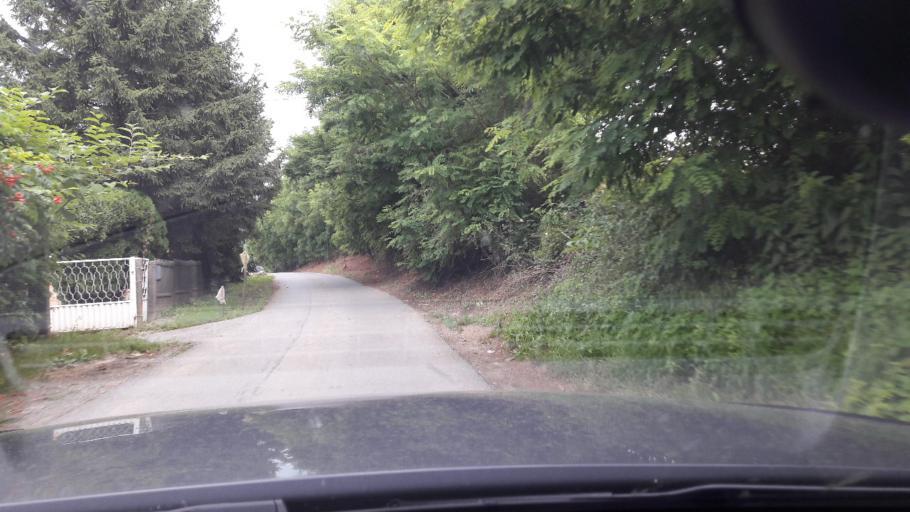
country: RS
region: Central Serbia
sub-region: Belgrade
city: Sopot
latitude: 44.6454
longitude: 20.5930
